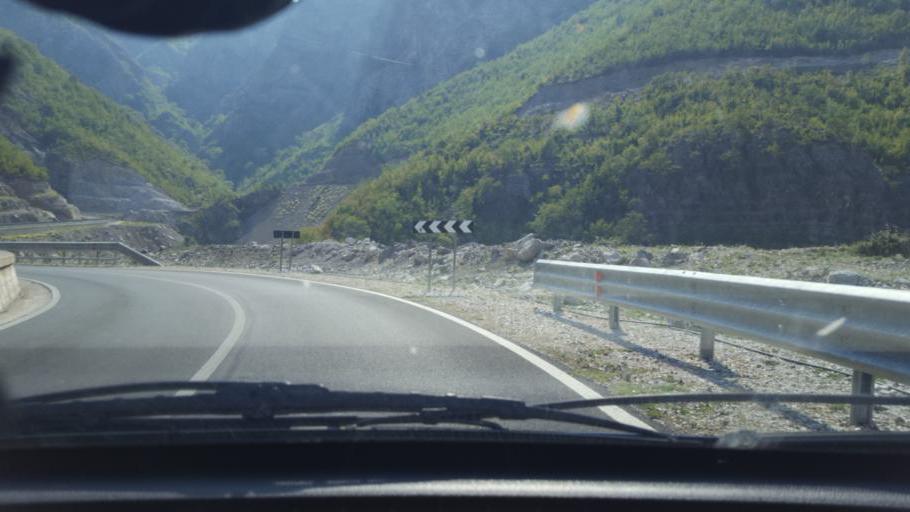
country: AL
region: Shkoder
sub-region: Rrethi i Malesia e Madhe
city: Kastrat
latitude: 42.4166
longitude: 19.5101
